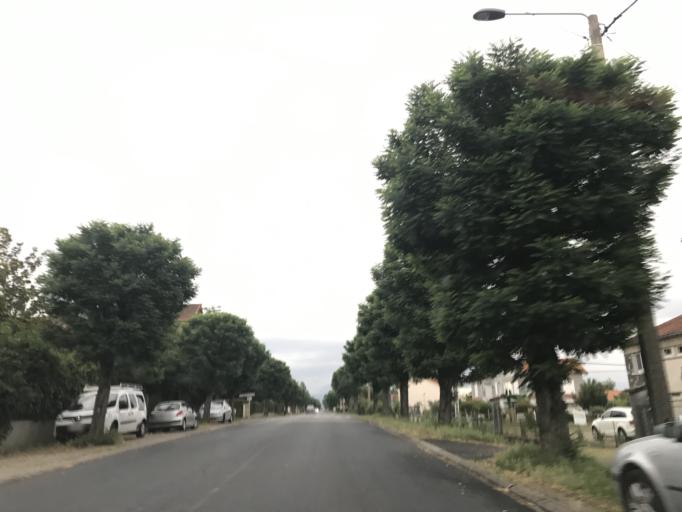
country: FR
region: Auvergne
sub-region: Departement du Puy-de-Dome
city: Lezoux
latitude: 45.8314
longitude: 3.3882
